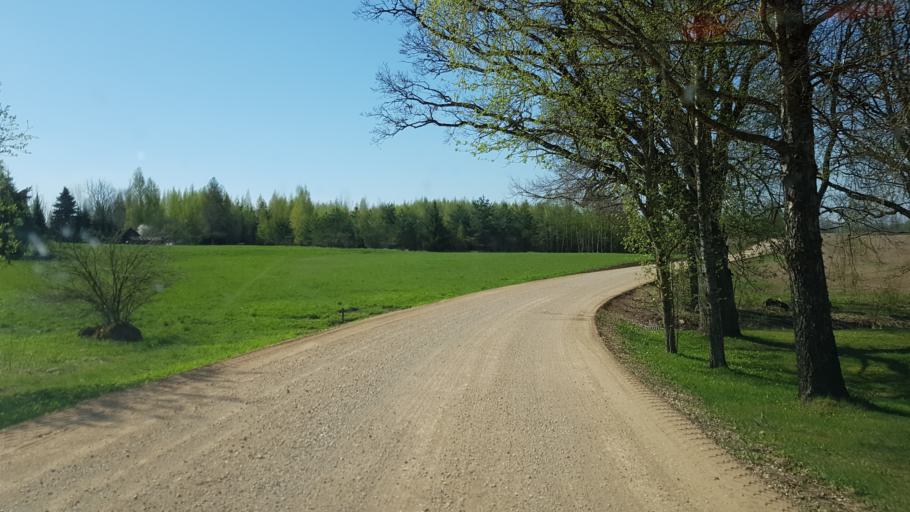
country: EE
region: Polvamaa
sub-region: Polva linn
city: Polva
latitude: 58.1090
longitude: 27.2392
